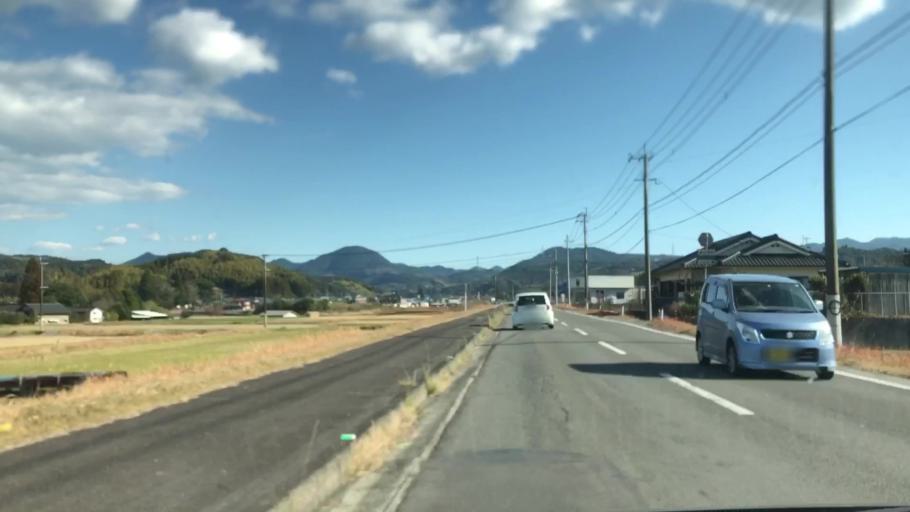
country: JP
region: Kagoshima
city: Satsumasendai
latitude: 31.7970
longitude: 130.4355
